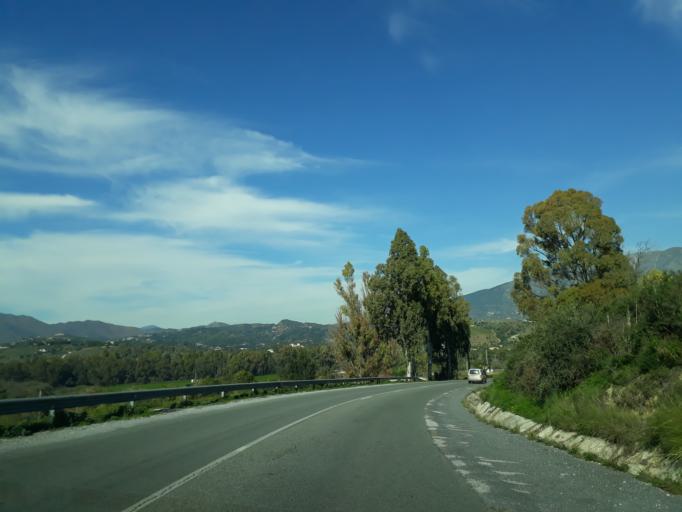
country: ES
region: Andalusia
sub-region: Provincia de Malaga
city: Fuengirola
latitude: 36.5382
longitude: -4.6876
